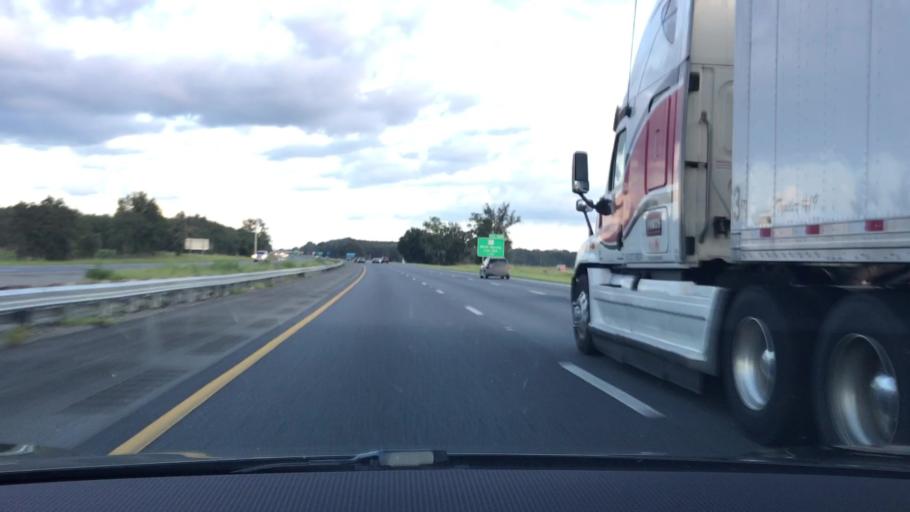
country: US
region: Florida
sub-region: Suwannee County
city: Wellborn
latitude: 30.3282
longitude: -82.8192
